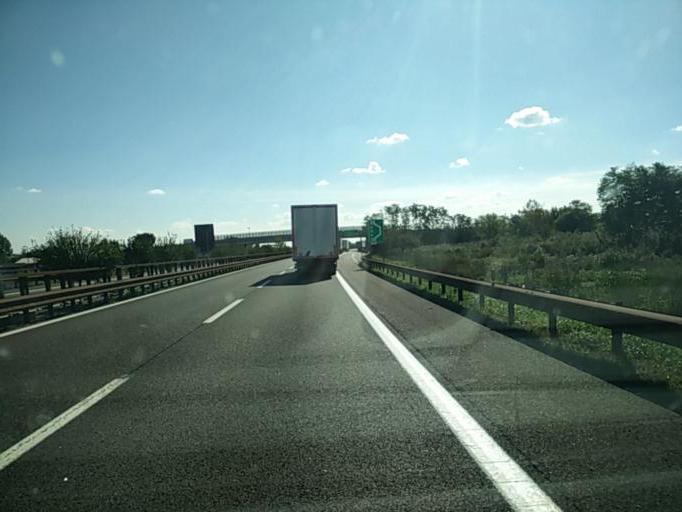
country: IT
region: Veneto
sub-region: Provincia di Verona
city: Caselle
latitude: 45.4179
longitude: 10.9139
